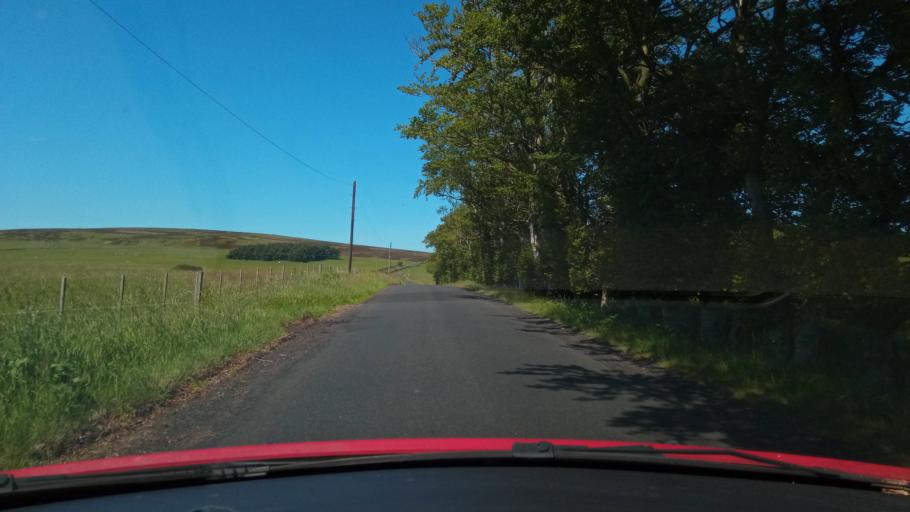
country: GB
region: Scotland
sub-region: The Scottish Borders
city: Duns
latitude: 55.8159
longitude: -2.5007
